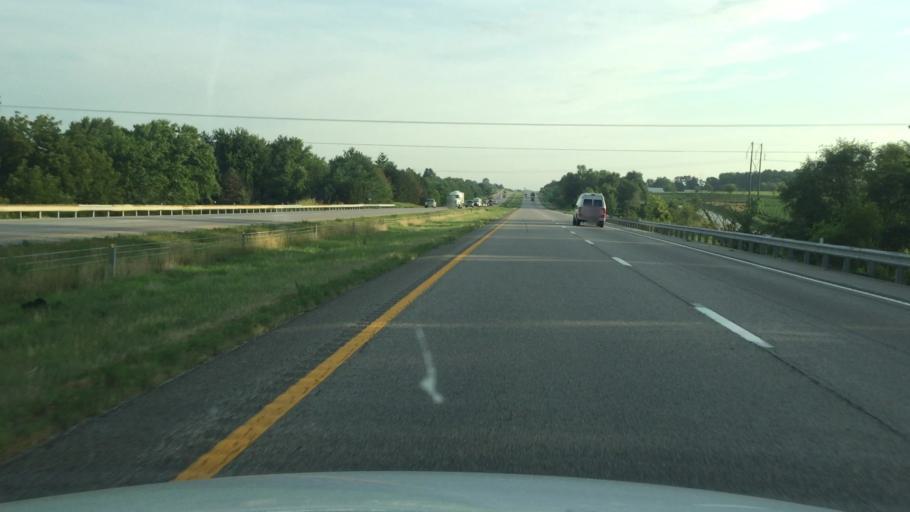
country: US
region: Missouri
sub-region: Clinton County
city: Gower
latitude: 39.5775
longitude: -94.7886
